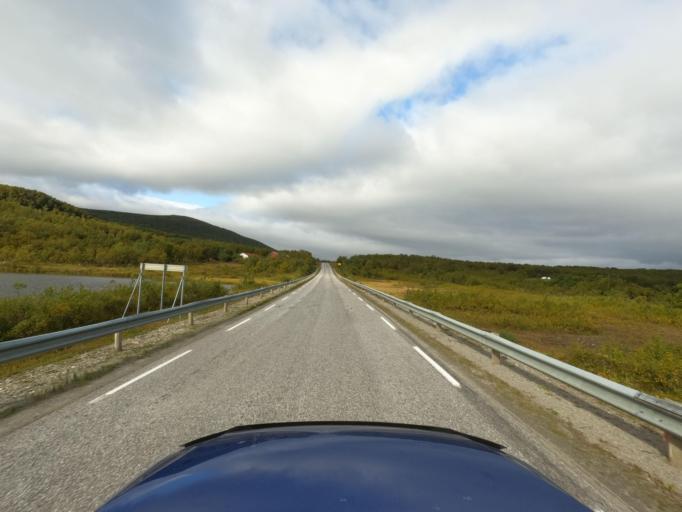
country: NO
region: Finnmark Fylke
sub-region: Porsanger
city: Lakselv
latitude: 70.2883
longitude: 25.0735
